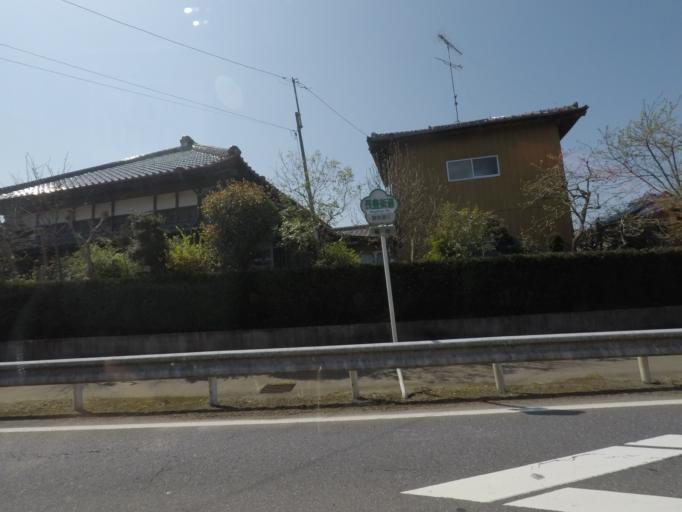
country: JP
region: Chiba
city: Narita
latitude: 35.8618
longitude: 140.2868
